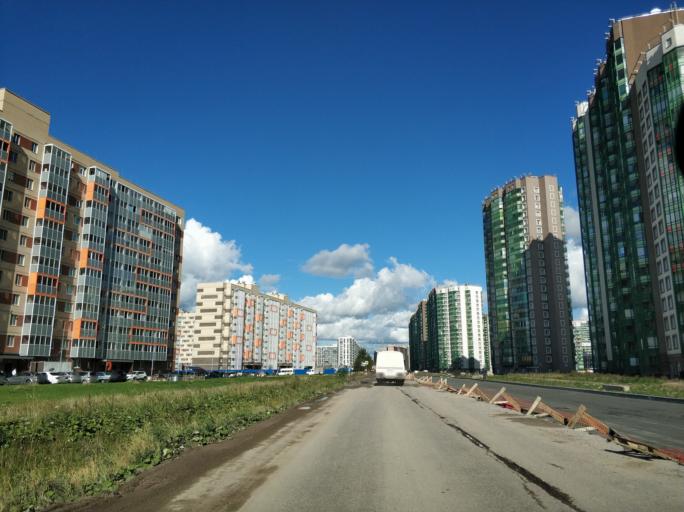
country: RU
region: St.-Petersburg
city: Grazhdanka
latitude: 60.0517
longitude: 30.4193
